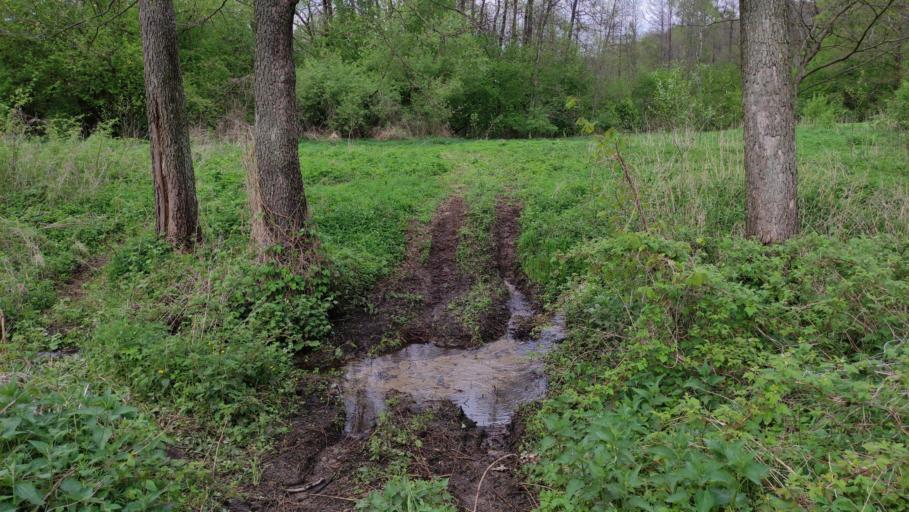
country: LT
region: Alytaus apskritis
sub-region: Alytus
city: Alytus
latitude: 54.4376
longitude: 24.0739
